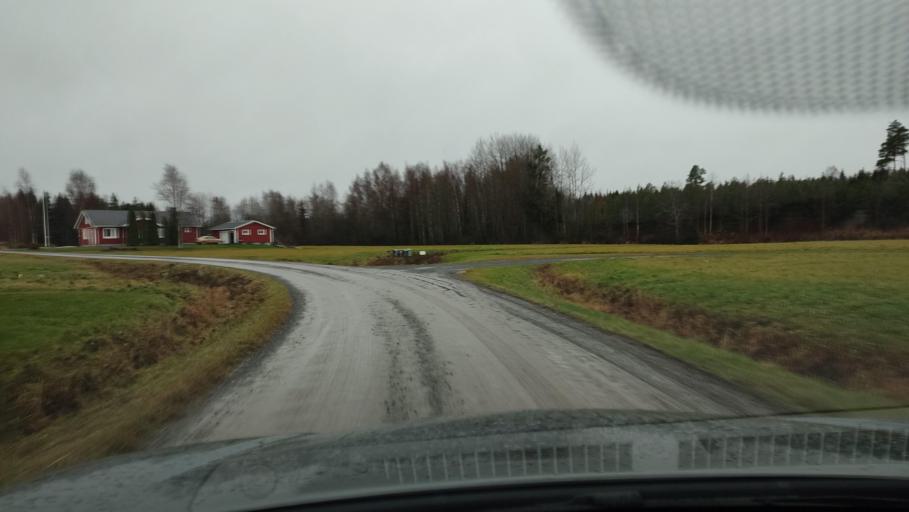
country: FI
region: Southern Ostrobothnia
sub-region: Suupohja
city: Karijoki
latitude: 62.2385
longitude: 21.5504
